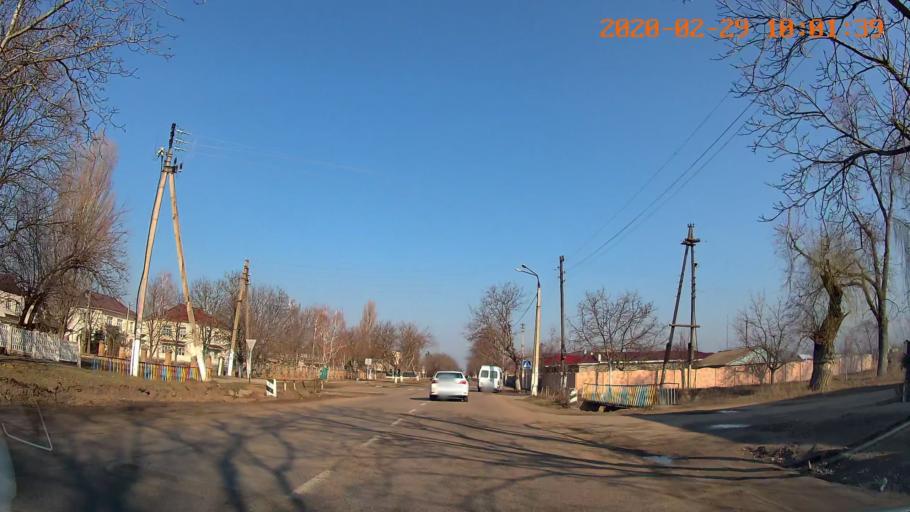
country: MD
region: Telenesti
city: Slobozia
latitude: 46.7768
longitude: 29.6845
